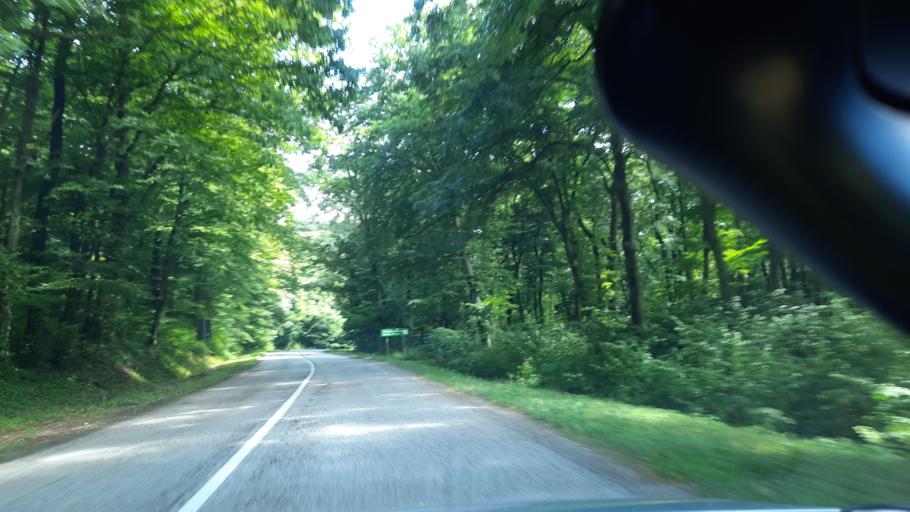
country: RS
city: Glozan
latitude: 45.1445
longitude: 19.5793
